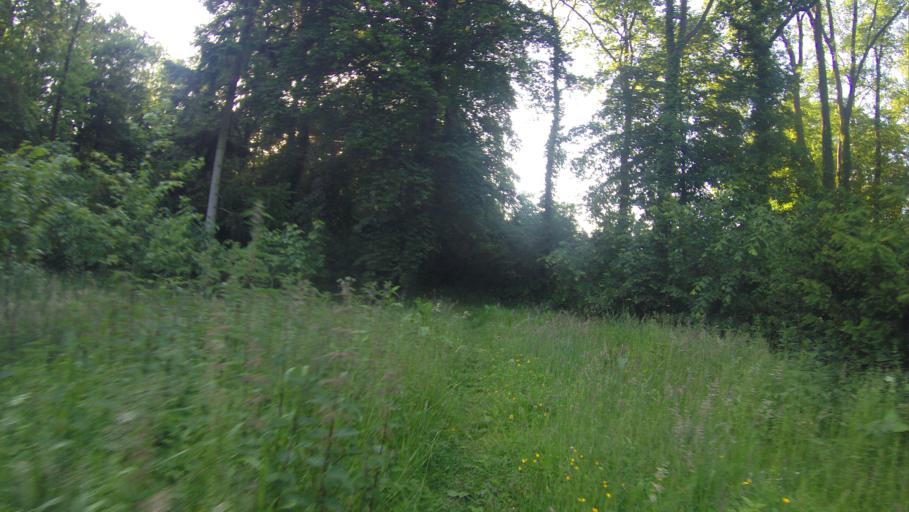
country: NL
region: Gelderland
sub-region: Gemeente Lochem
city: Lochem
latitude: 52.1184
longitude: 6.3871
